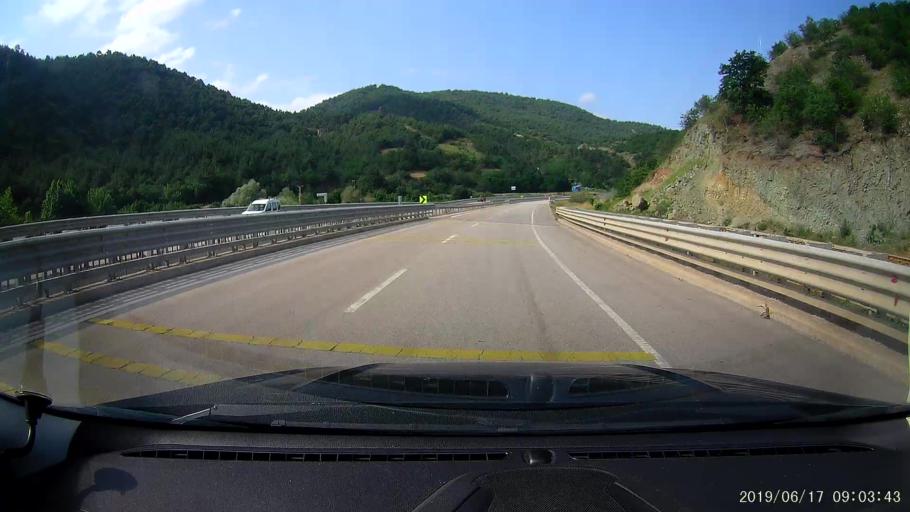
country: TR
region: Amasya
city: Tasova
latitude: 40.7513
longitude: 36.3018
